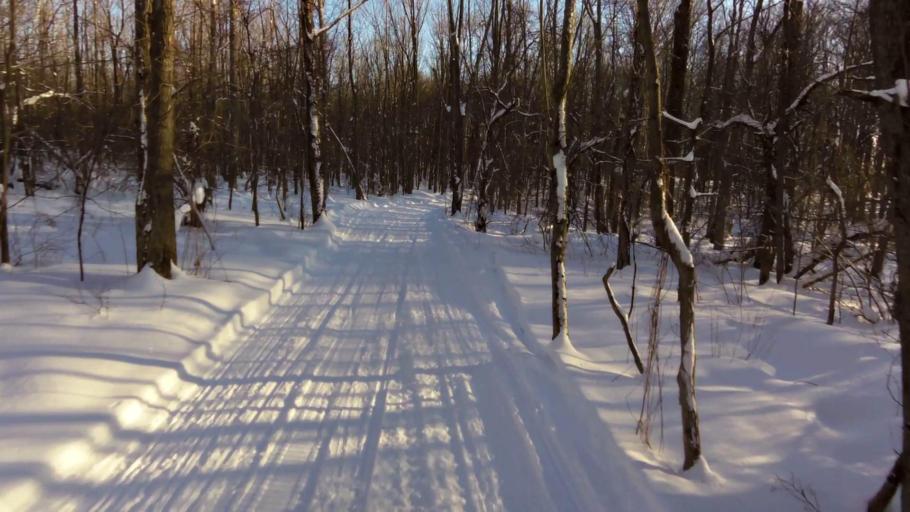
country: US
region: New York
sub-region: Chautauqua County
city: Mayville
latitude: 42.2469
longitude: -79.3918
